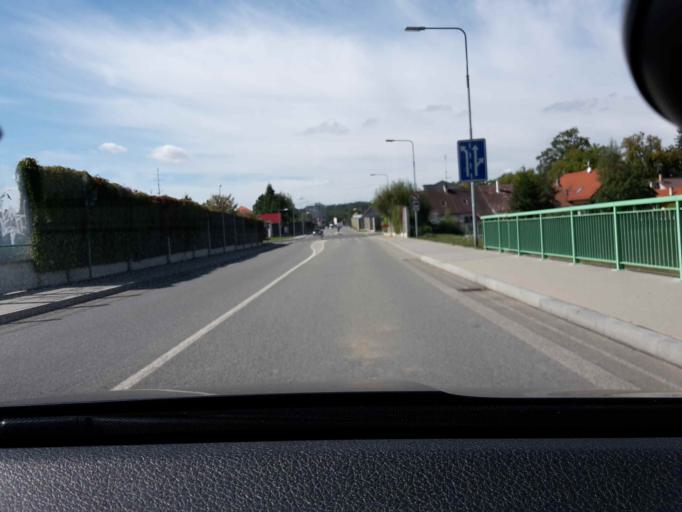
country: CZ
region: Jihocesky
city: Sobeslav
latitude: 49.2634
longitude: 14.7182
